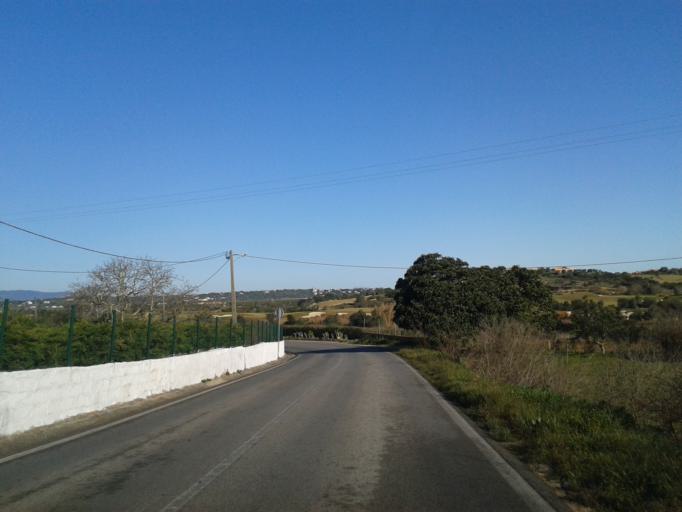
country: PT
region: Faro
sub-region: Silves
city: Armacao de Pera
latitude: 37.1393
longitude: -8.3587
